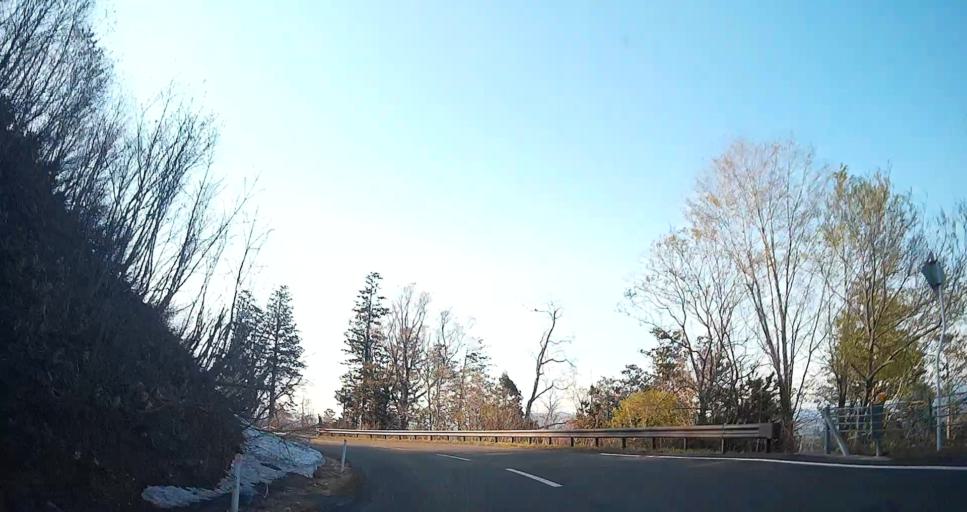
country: JP
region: Aomori
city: Mutsu
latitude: 41.3116
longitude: 141.1129
